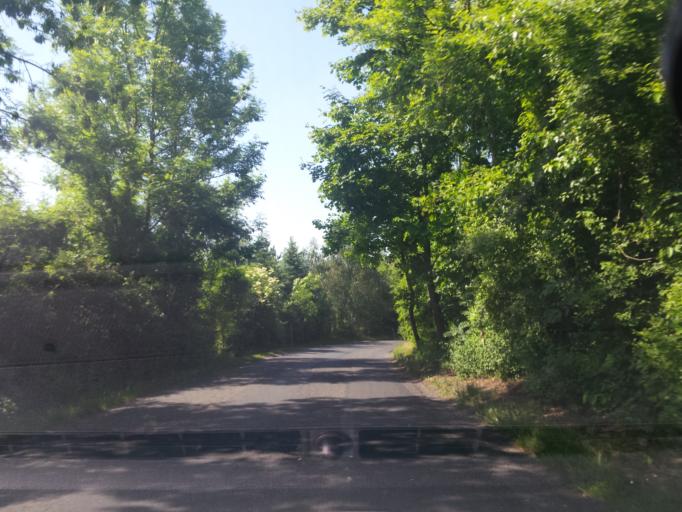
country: CZ
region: Central Bohemia
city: Nelahozeves
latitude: 50.2580
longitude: 14.2967
